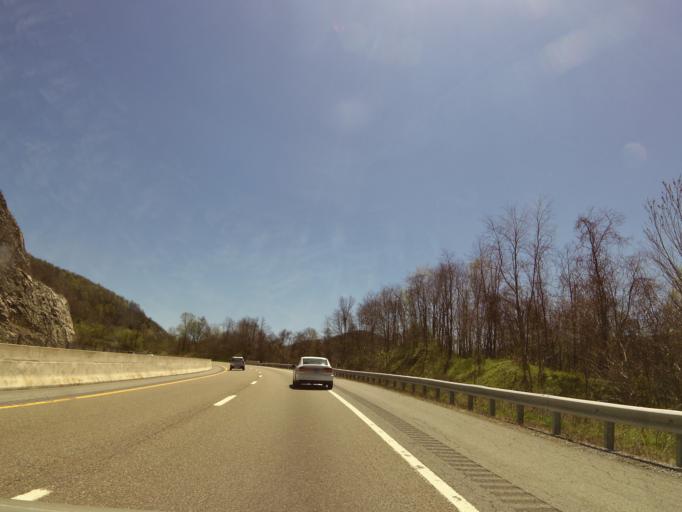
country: US
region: North Carolina
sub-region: Madison County
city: Mars Hill
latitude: 35.9661
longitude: -82.5552
